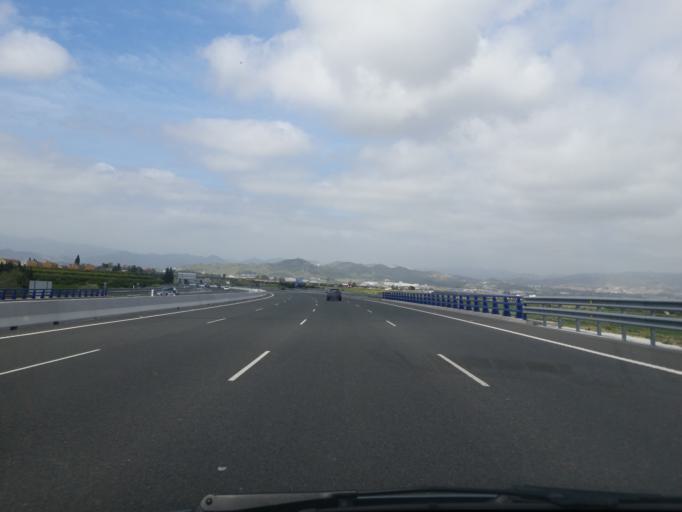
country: ES
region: Andalusia
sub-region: Provincia de Malaga
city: Alhaurin de la Torre
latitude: 36.6779
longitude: -4.5259
